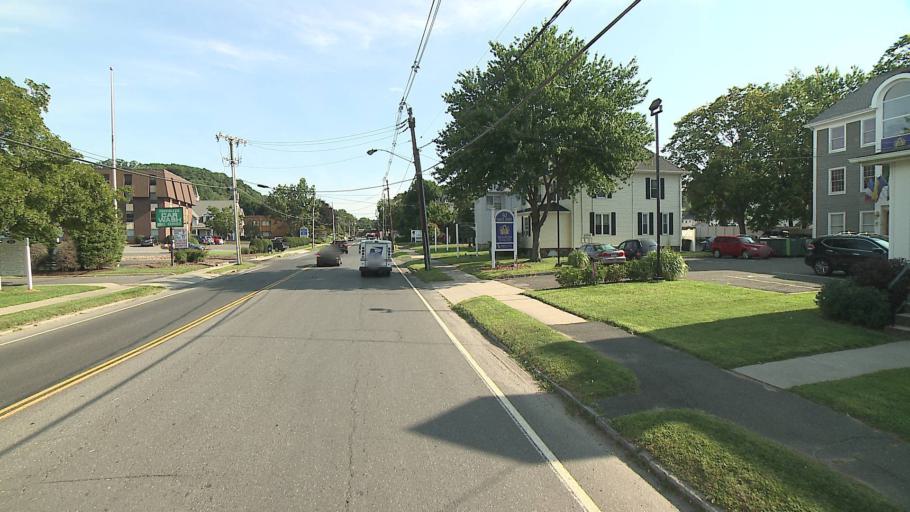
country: US
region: Connecticut
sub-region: Fairfield County
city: Danbury
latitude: 41.4058
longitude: -73.4564
